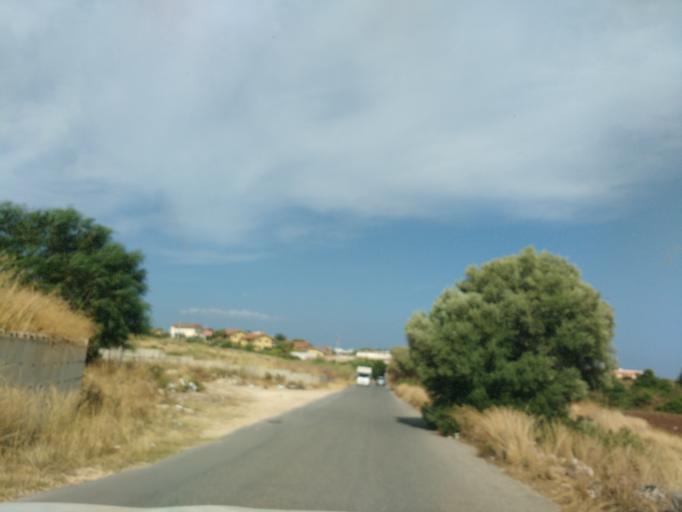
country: IT
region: Sicily
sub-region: Provincia di Siracusa
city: Noto
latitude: 36.8508
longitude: 15.1045
